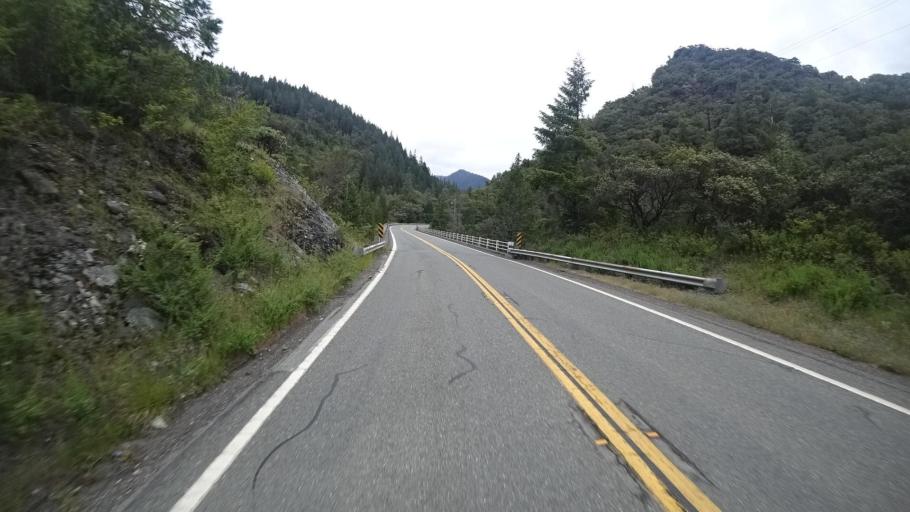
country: US
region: California
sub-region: Humboldt County
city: Willow Creek
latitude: 41.2316
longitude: -123.6590
